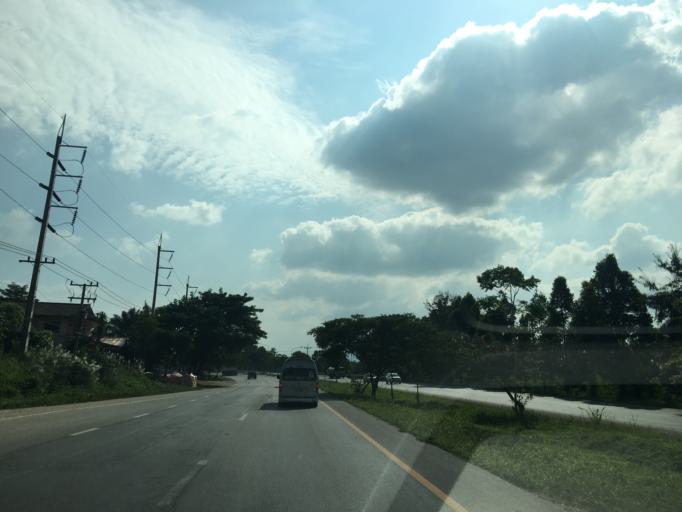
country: TH
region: Chiang Rai
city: Mae Lao
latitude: 19.7074
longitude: 99.7198
